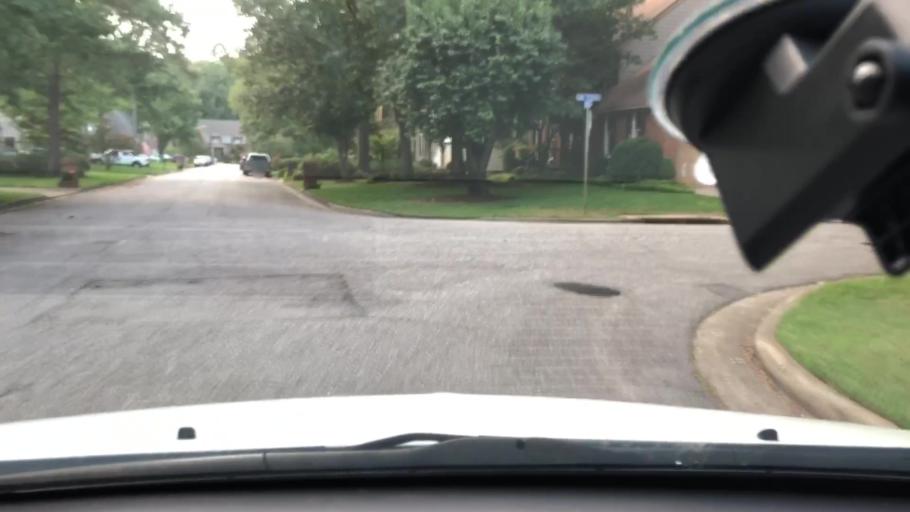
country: US
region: Virginia
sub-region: City of Chesapeake
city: Chesapeake
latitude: 36.7021
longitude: -76.2897
